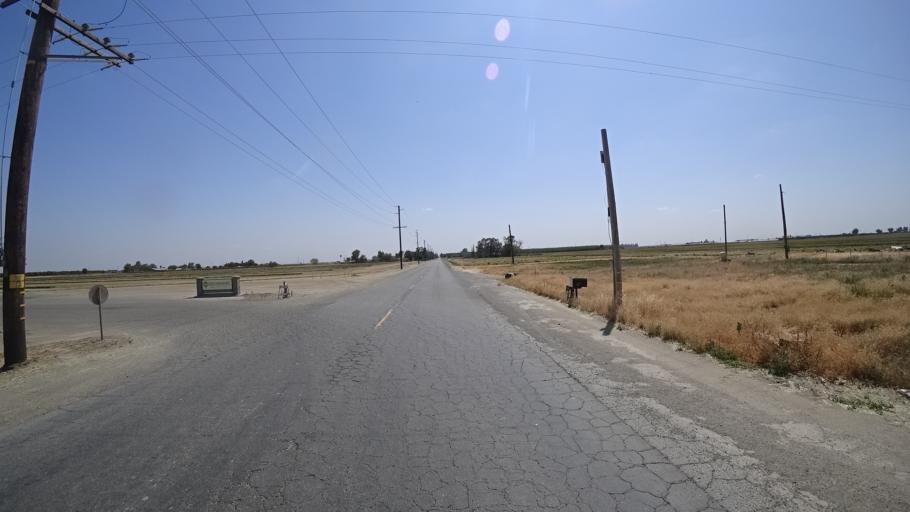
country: US
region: California
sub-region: Kings County
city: Home Garden
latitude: 36.3135
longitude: -119.5919
